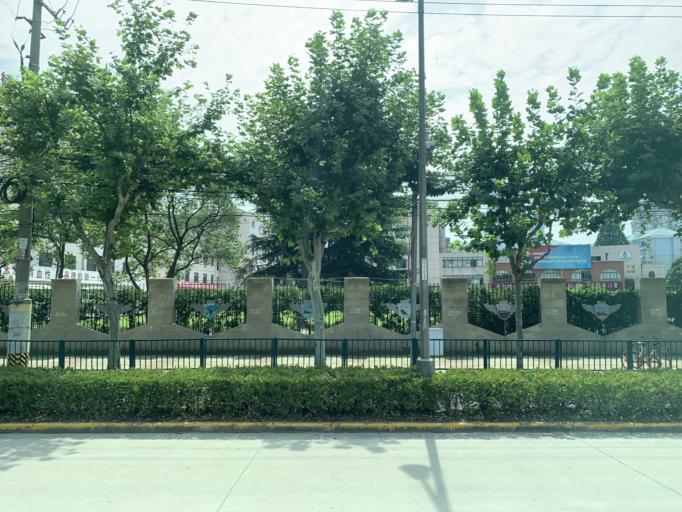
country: CN
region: Shanghai Shi
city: Pudong
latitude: 31.2394
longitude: 121.5270
